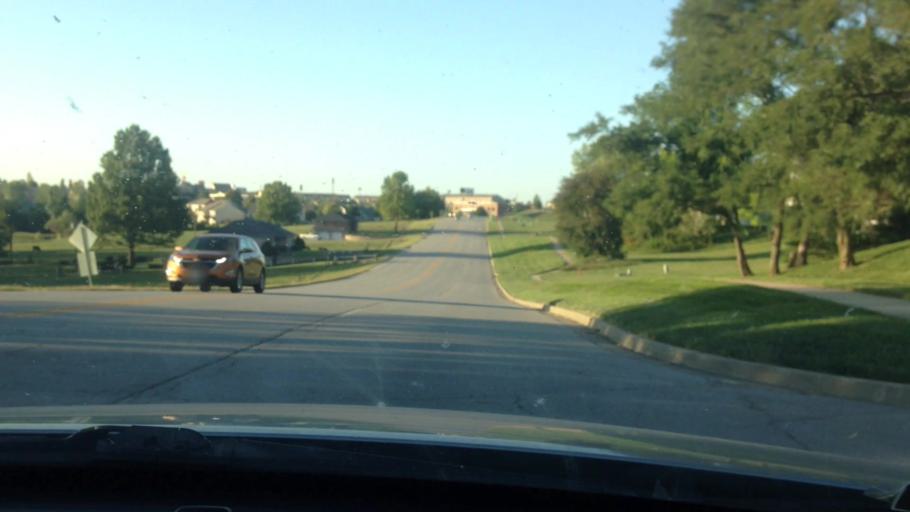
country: US
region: Missouri
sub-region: Platte County
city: Platte City
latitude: 39.3433
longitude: -94.7611
